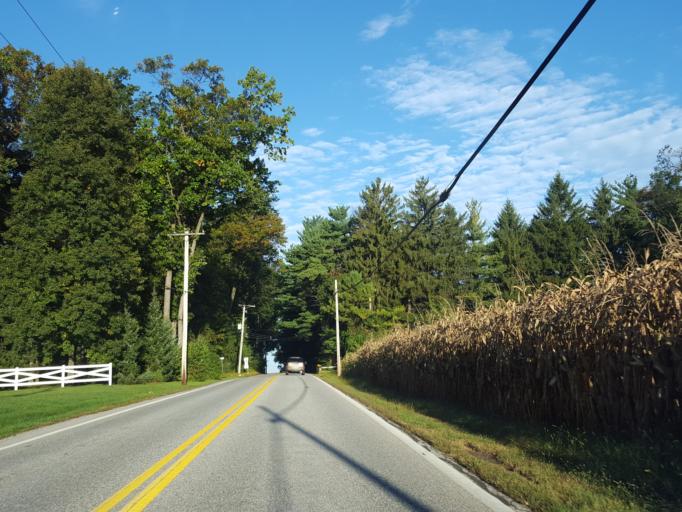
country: US
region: Pennsylvania
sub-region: York County
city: Stonybrook
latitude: 39.9723
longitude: -76.6171
